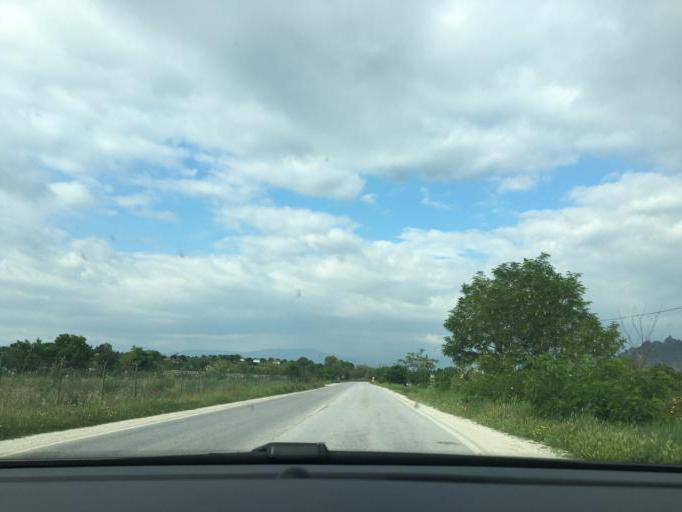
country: MK
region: Prilep
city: Prilep
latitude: 41.3606
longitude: 21.5936
